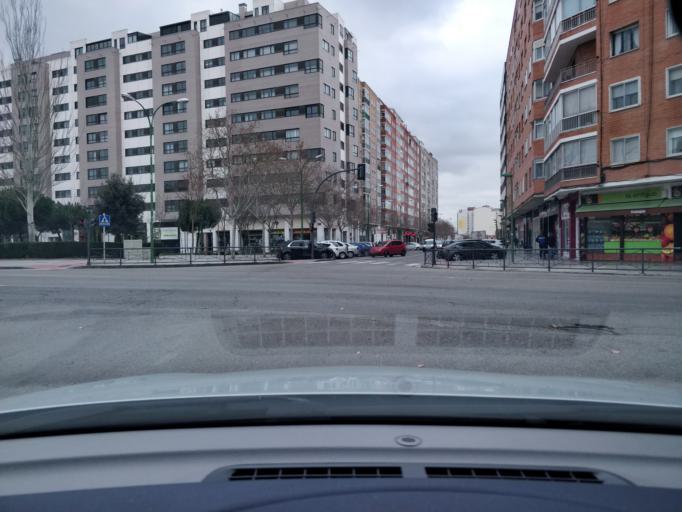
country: ES
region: Castille and Leon
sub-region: Provincia de Burgos
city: Burgos
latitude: 42.3566
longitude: -3.6638
